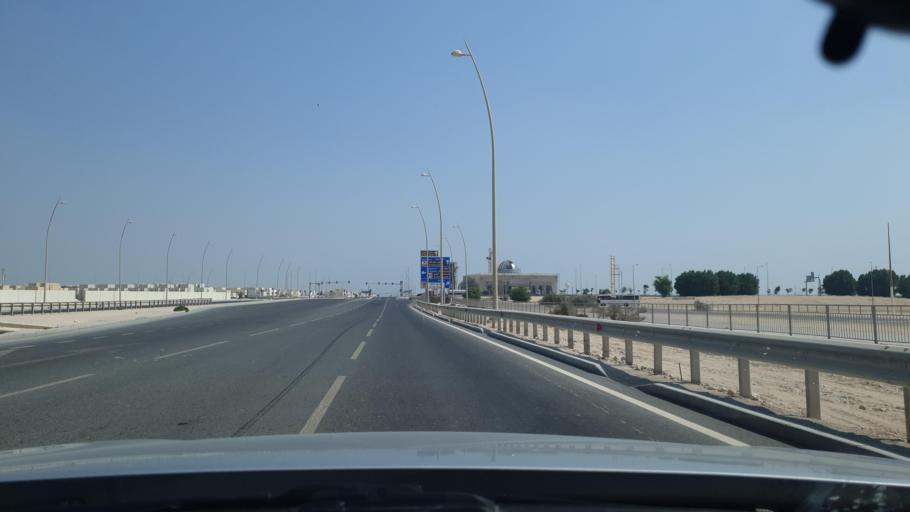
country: QA
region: Al Khawr
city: Al Khawr
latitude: 25.6628
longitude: 51.4974
